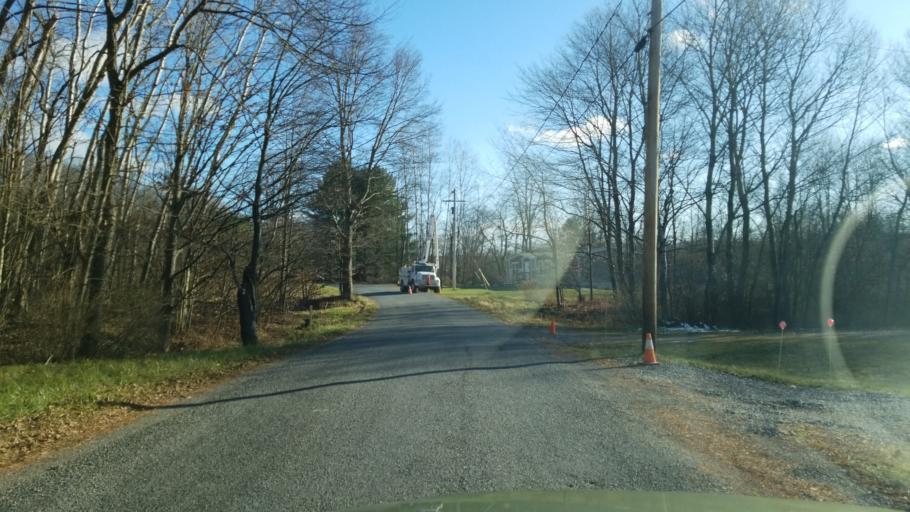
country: US
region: Pennsylvania
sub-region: Jefferson County
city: Brockway
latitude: 41.2624
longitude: -78.8036
